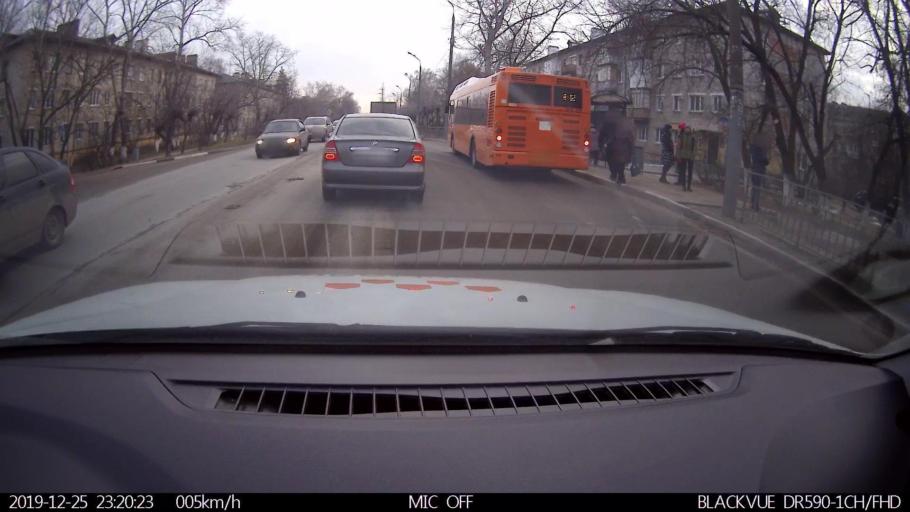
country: RU
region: Nizjnij Novgorod
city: Gorbatovka
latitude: 56.3535
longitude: 43.8327
